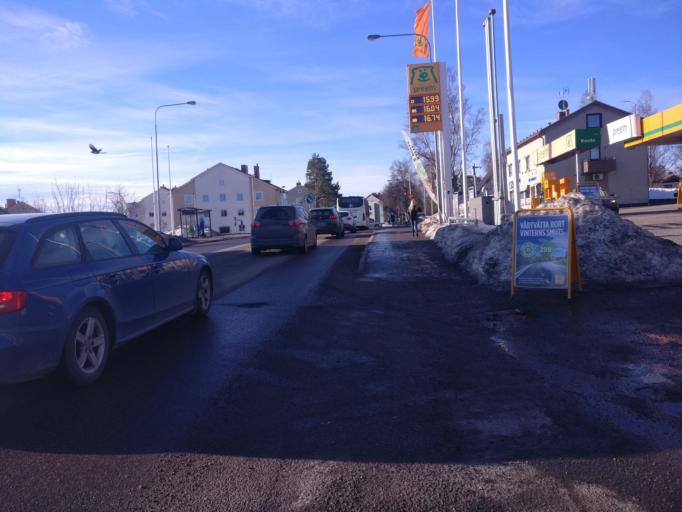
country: SE
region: Vaesternorrland
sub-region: Sundsvalls Kommun
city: Sundsvall
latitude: 62.4015
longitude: 17.3282
